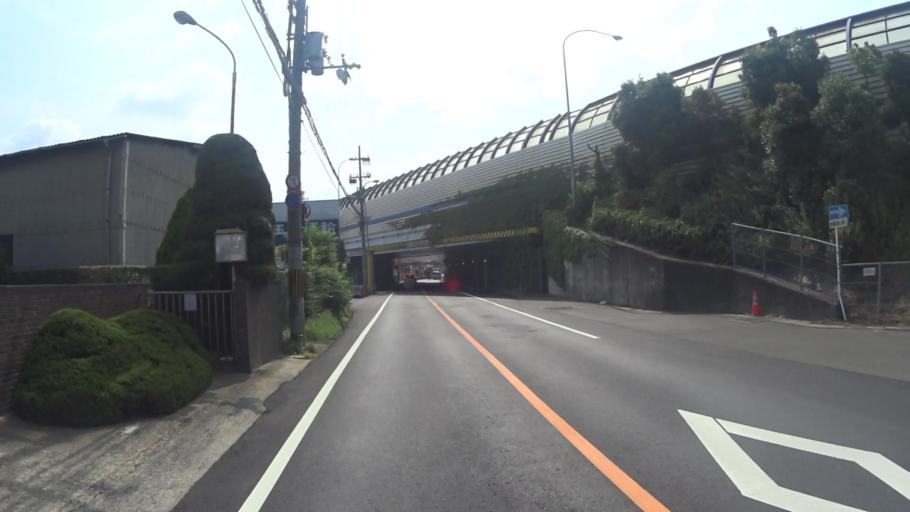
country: JP
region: Kyoto
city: Muko
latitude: 34.9477
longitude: 135.7281
